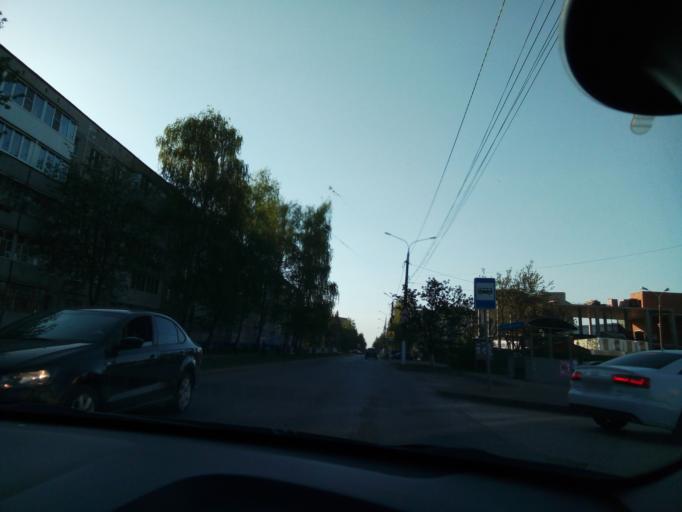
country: RU
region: Chuvashia
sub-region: Cheboksarskiy Rayon
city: Cheboksary
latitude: 56.1442
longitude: 47.1946
